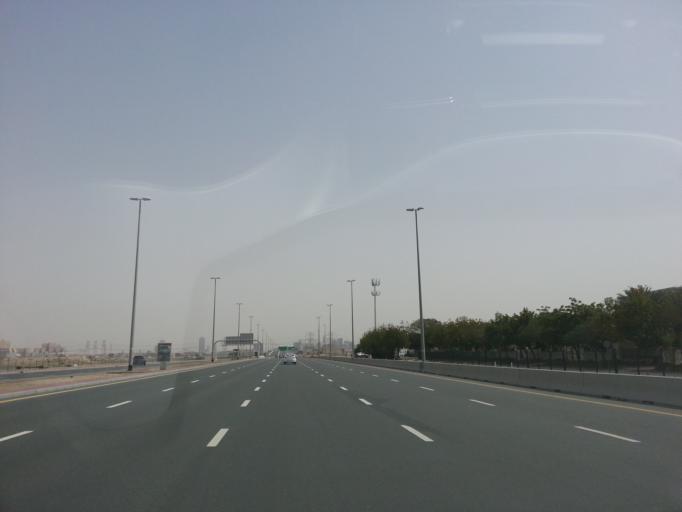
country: AE
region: Dubai
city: Dubai
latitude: 25.0755
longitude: 55.1839
